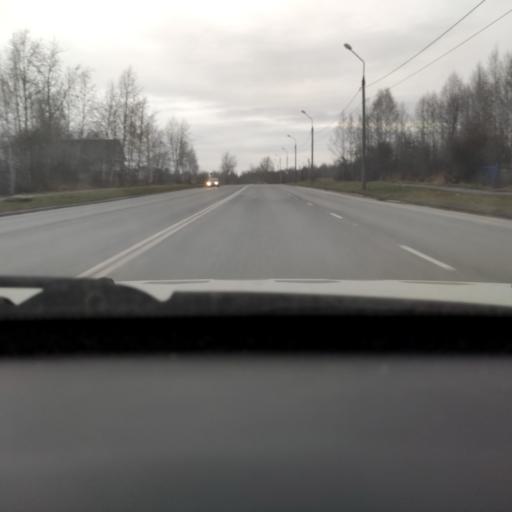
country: RU
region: Perm
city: Polazna
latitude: 58.1252
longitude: 56.4051
